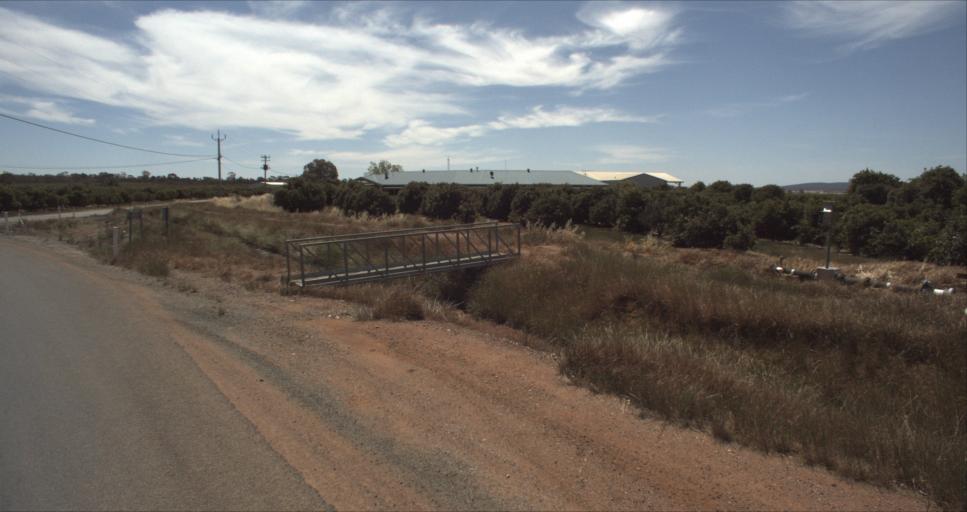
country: AU
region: New South Wales
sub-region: Leeton
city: Leeton
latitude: -34.5914
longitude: 146.4636
